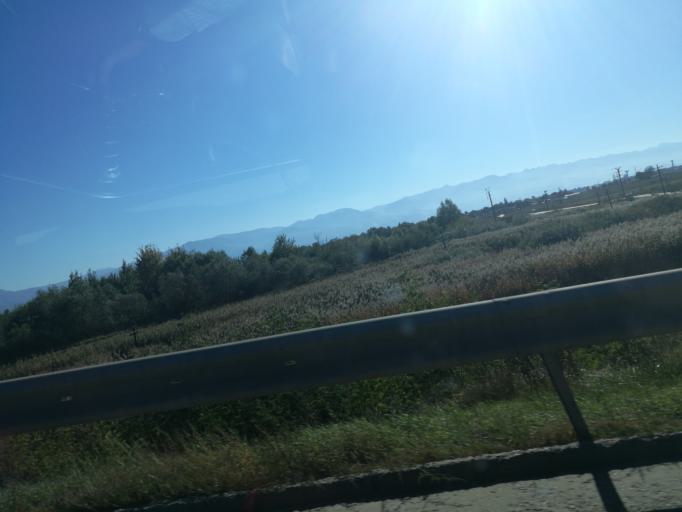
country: RO
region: Brasov
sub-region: Comuna Mandra
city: Mandra
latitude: 45.8320
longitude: 25.0151
